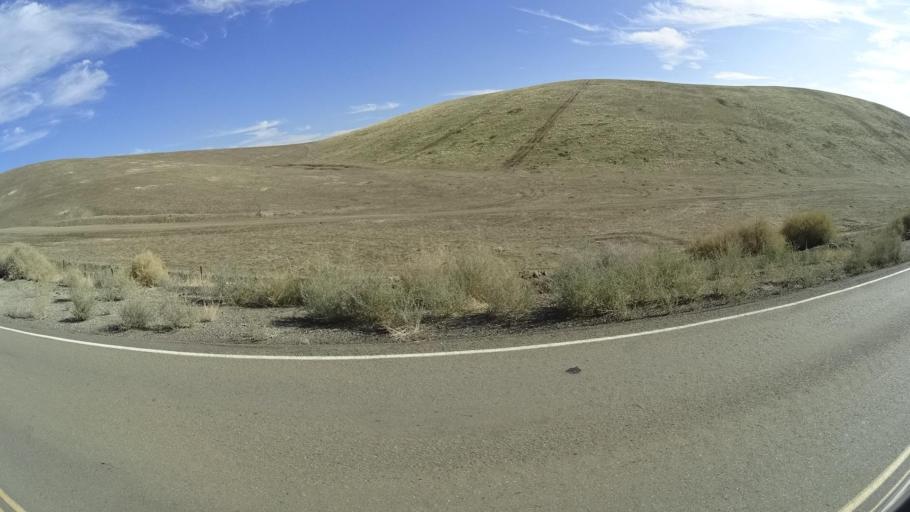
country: US
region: California
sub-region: Kern County
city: Oildale
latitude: 35.5972
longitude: -118.9498
